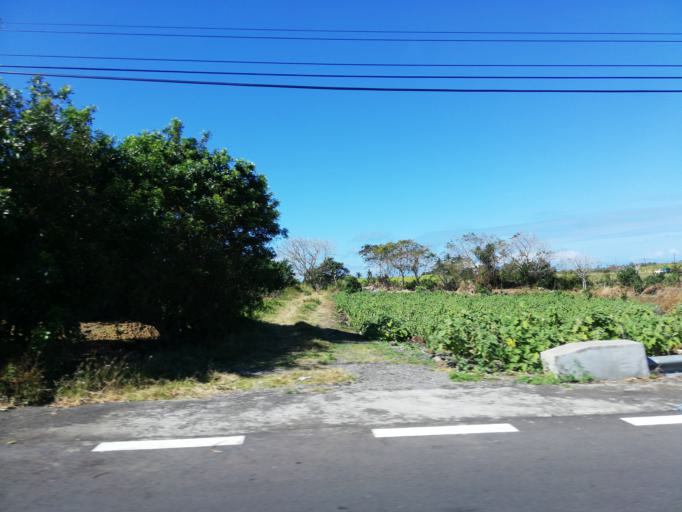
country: MU
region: Grand Port
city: Plaine Magnien
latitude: -20.4440
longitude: 57.6907
